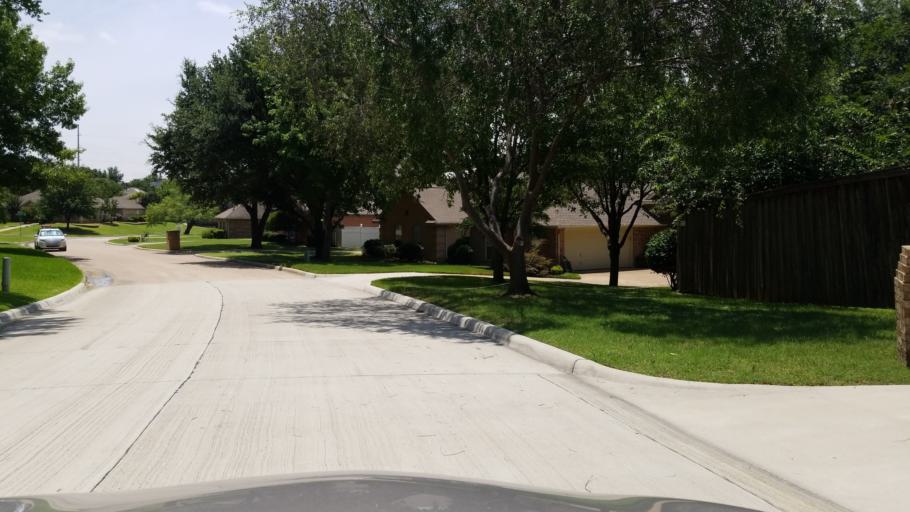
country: US
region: Texas
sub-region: Dallas County
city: Grand Prairie
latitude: 32.6831
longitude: -96.9889
